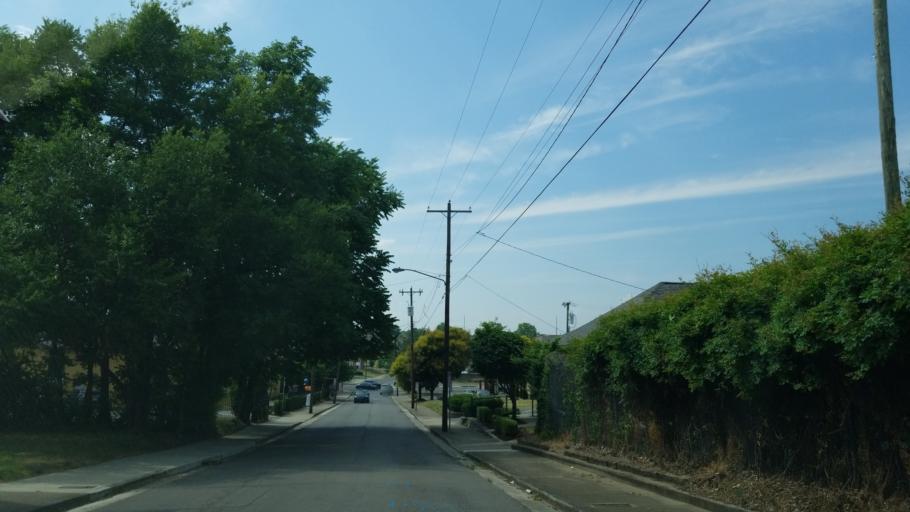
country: US
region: Tennessee
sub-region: Davidson County
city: Nashville
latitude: 36.1585
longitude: -86.7950
